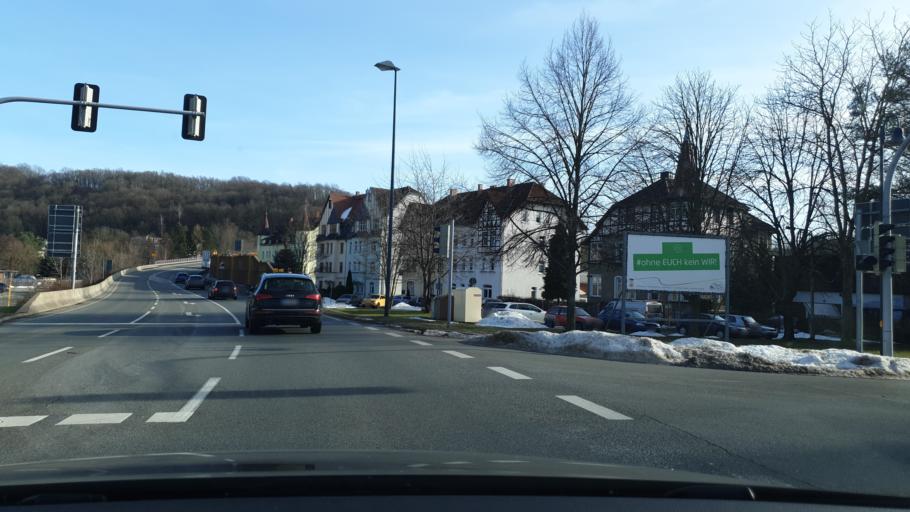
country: DE
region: Thuringia
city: Weida
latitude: 50.7797
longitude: 12.0643
